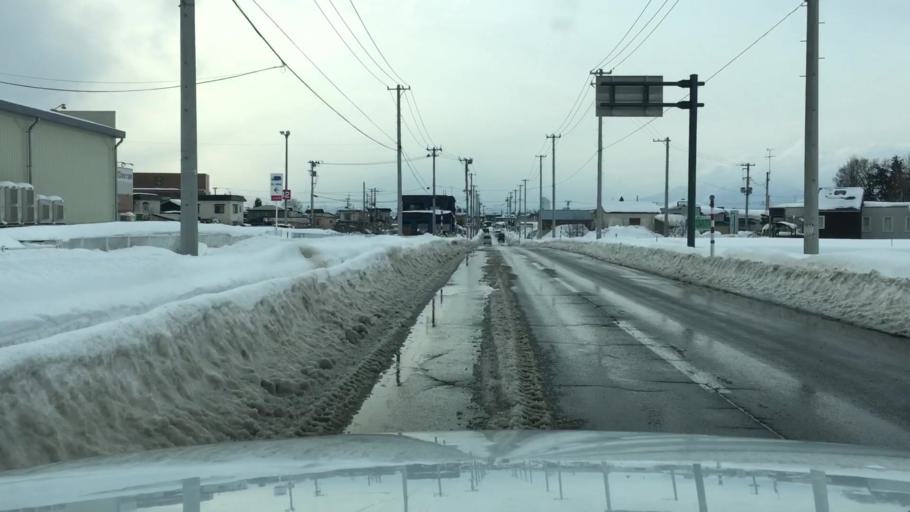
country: JP
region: Aomori
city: Kuroishi
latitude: 40.5918
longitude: 140.5671
